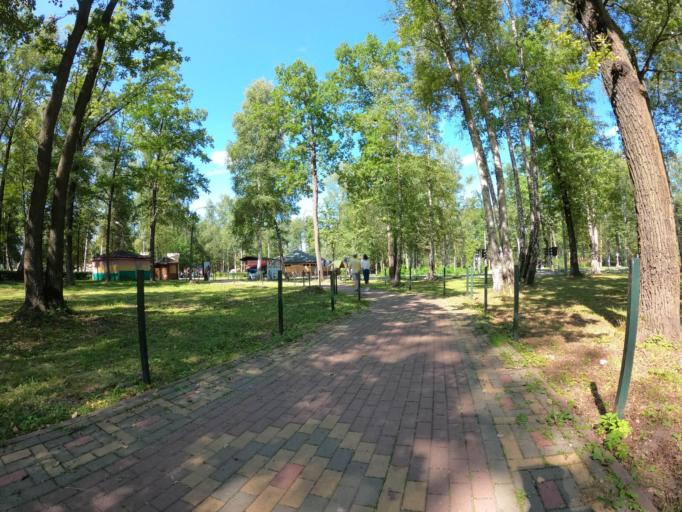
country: RU
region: Moskovskaya
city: Stupino
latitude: 54.8816
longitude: 38.0853
